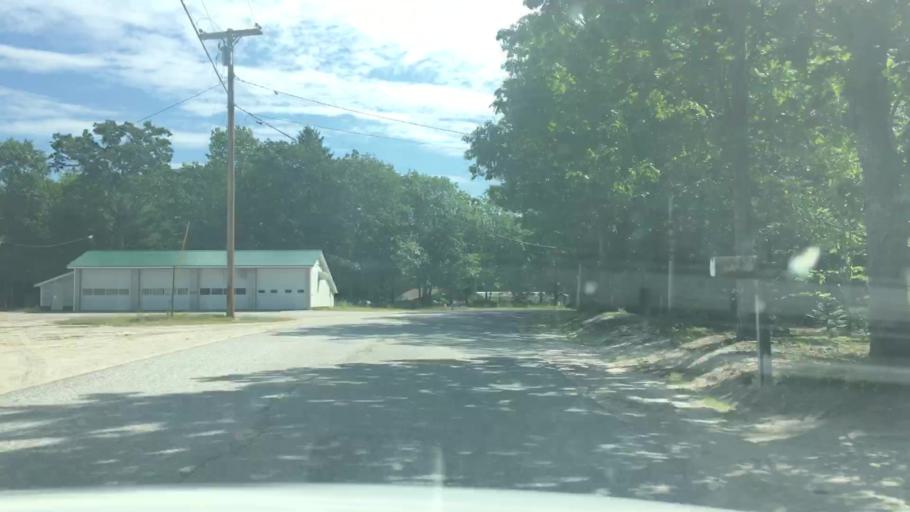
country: US
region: Maine
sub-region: Androscoggin County
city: Turner
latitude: 44.1920
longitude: -70.2448
